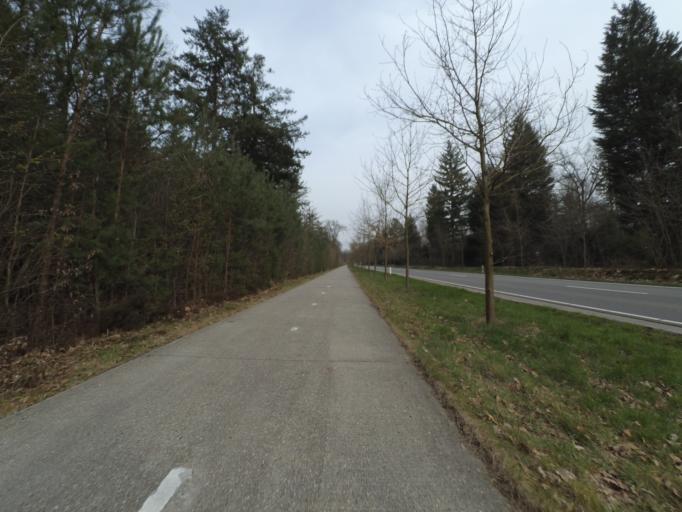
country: NL
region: Gelderland
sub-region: Gemeente Arnhem
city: Hoogkamp
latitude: 52.0321
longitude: 5.8607
